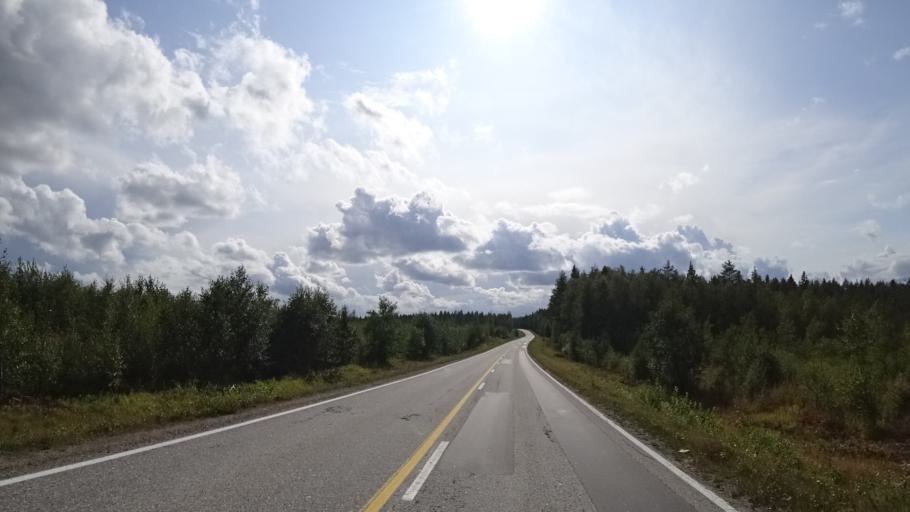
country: FI
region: North Karelia
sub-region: Joensuu
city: Ilomantsi
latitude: 62.6984
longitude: 30.9930
